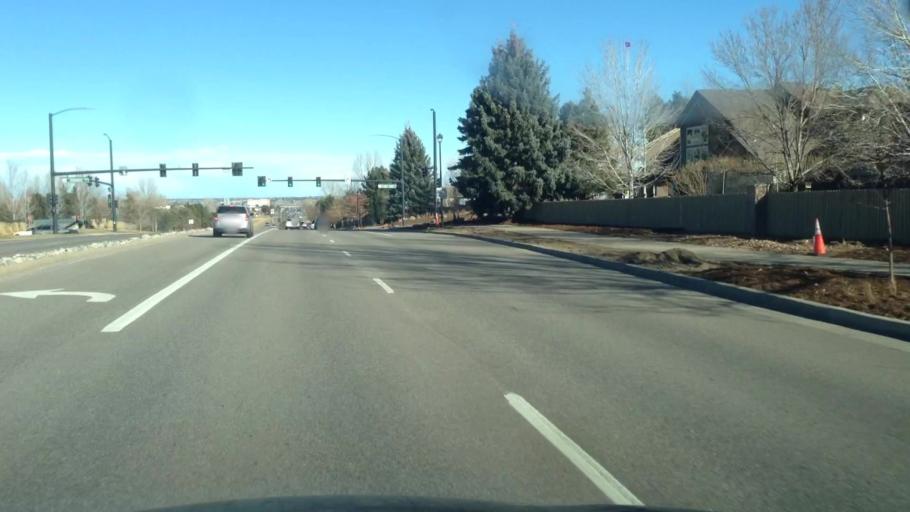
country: US
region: Colorado
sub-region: Douglas County
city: Stonegate
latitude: 39.5229
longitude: -104.7934
